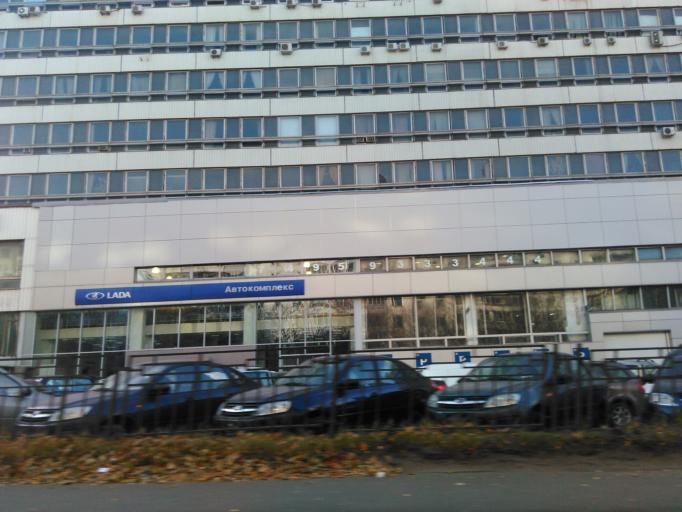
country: RU
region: Moscow
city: Ostankinskiy
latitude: 55.8191
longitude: 37.6203
